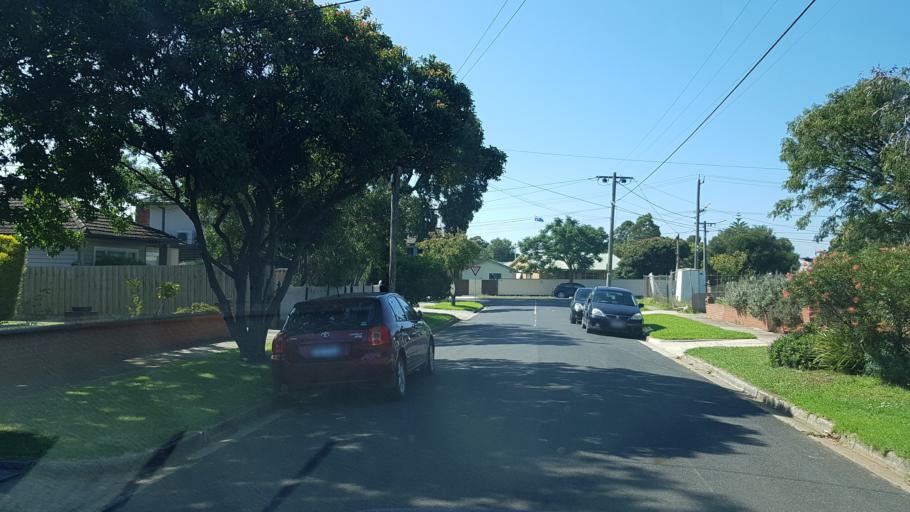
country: AU
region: Victoria
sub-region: Banyule
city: Heidelberg Heights
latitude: -37.7471
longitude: 145.0480
